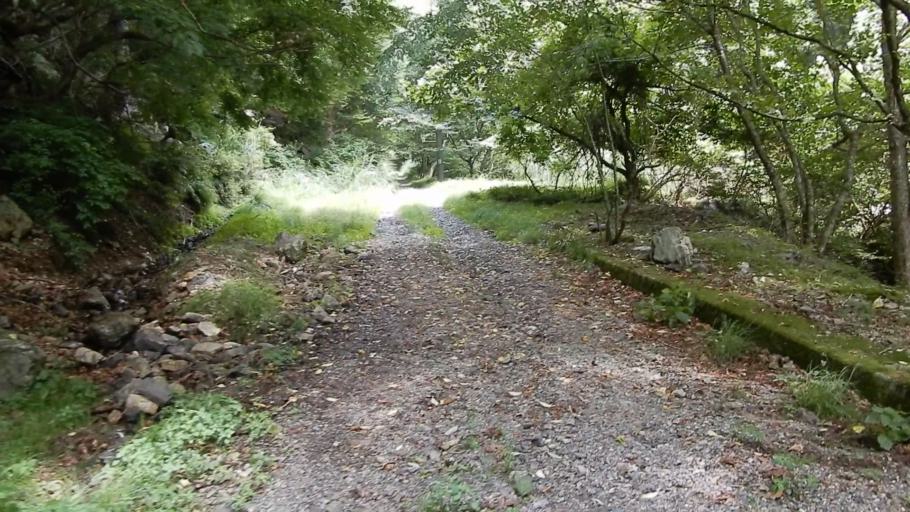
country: JP
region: Saitama
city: Chichibu
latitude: 35.9114
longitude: 139.0986
